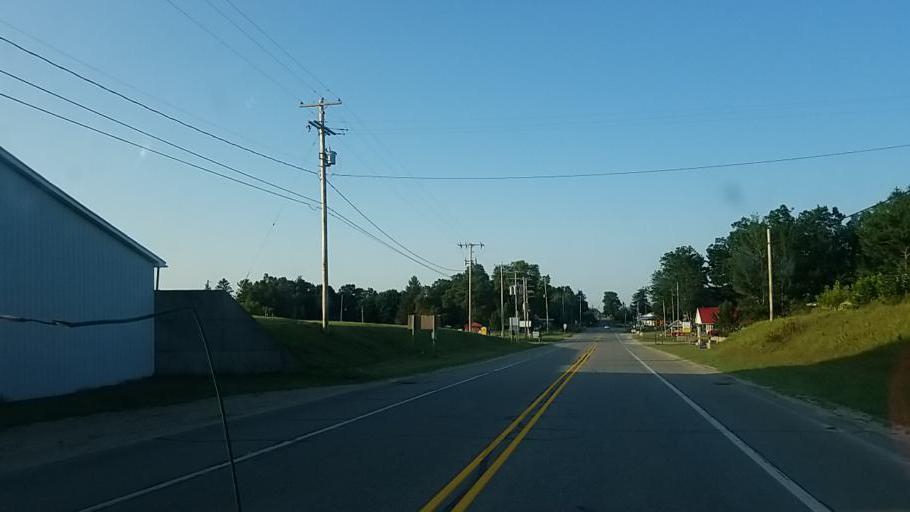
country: US
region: Michigan
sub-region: Montcalm County
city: Edmore
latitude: 43.4296
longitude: -85.1490
